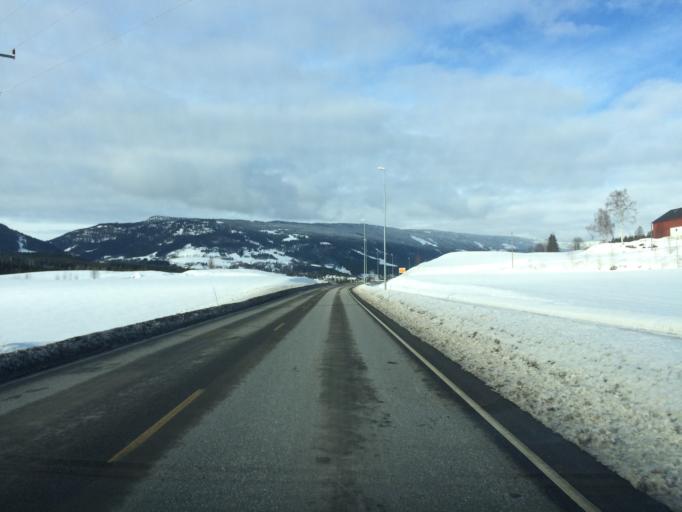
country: NO
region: Oppland
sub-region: Gausdal
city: Segalstad bru
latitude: 61.2209
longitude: 10.2448
